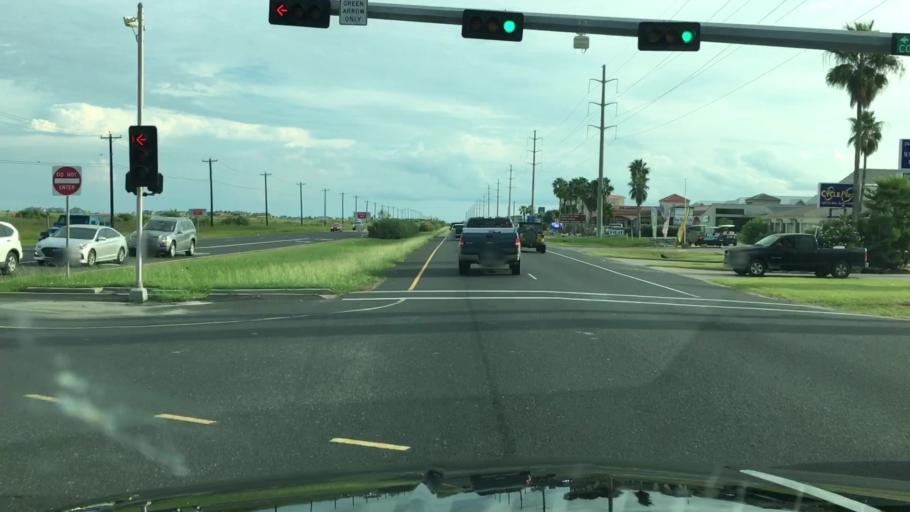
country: US
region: Texas
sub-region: Nueces County
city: Corpus Christi
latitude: 27.6179
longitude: -97.2219
